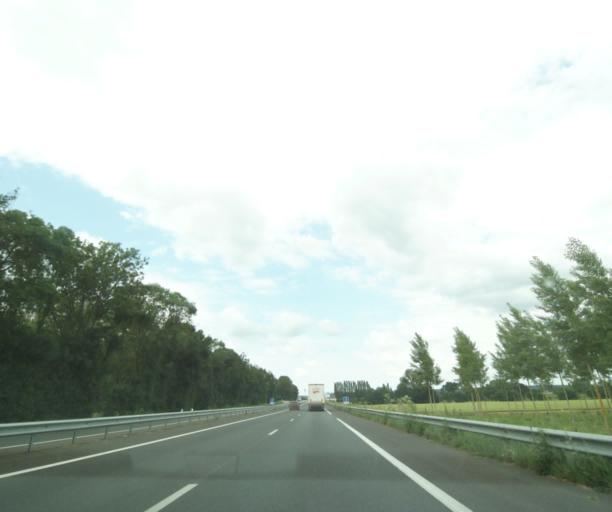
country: FR
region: Pays de la Loire
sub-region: Departement de Maine-et-Loire
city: Vivy
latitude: 47.2994
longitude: -0.0386
